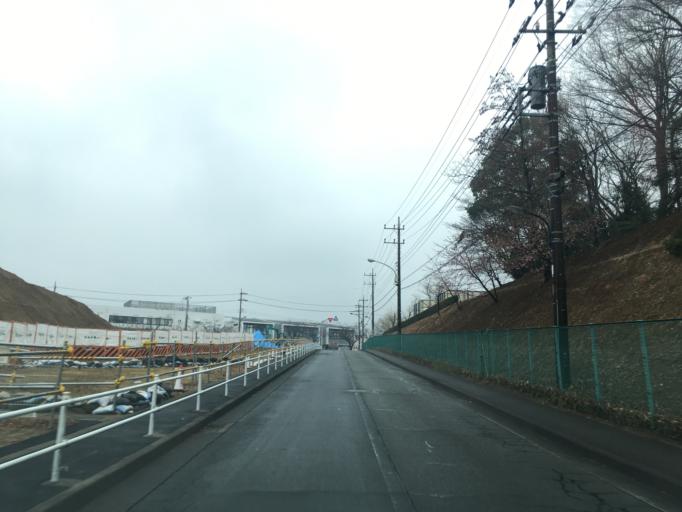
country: JP
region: Tokyo
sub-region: Machida-shi
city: Machida
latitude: 35.5871
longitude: 139.4104
